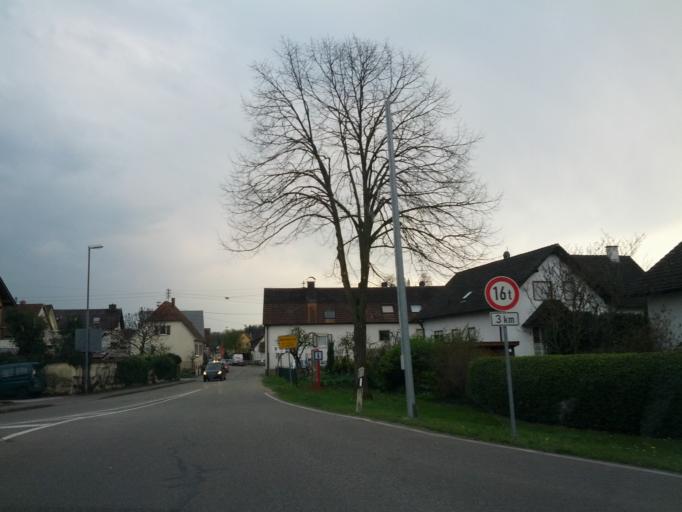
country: DE
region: Baden-Wuerttemberg
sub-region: Freiburg Region
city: Eichstetten
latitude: 48.1078
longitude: 7.7779
